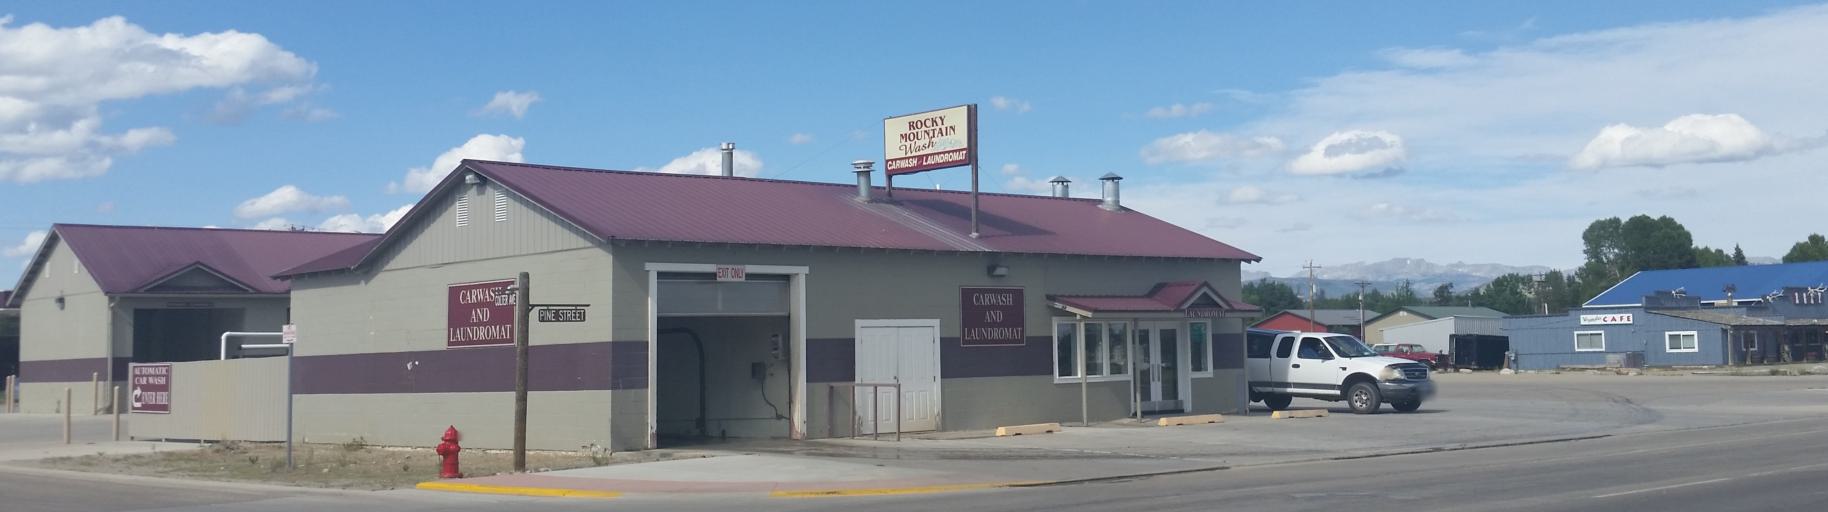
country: US
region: Wyoming
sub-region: Sublette County
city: Pinedale
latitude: 42.8666
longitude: -109.8755
